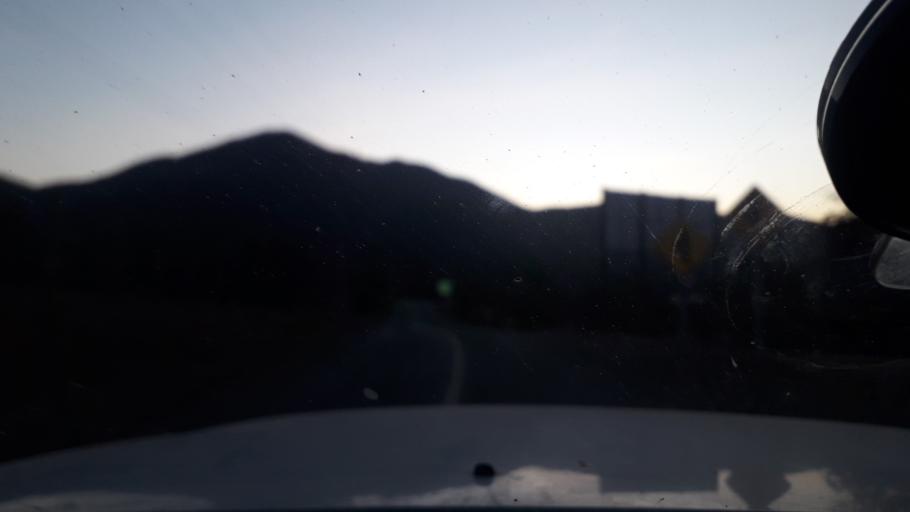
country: CL
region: Valparaiso
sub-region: Provincia de Marga Marga
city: Limache
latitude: -33.1768
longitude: -71.1220
